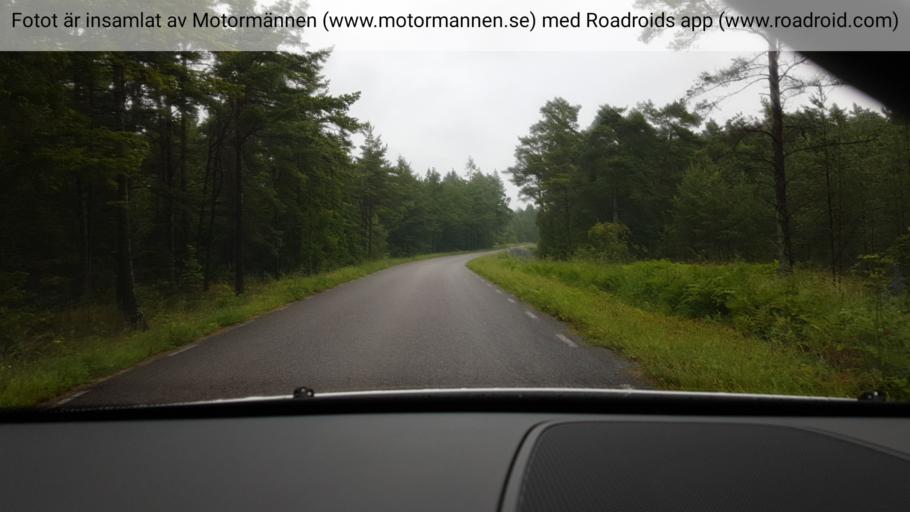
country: SE
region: Gotland
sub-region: Gotland
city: Slite
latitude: 57.8554
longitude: 18.7750
